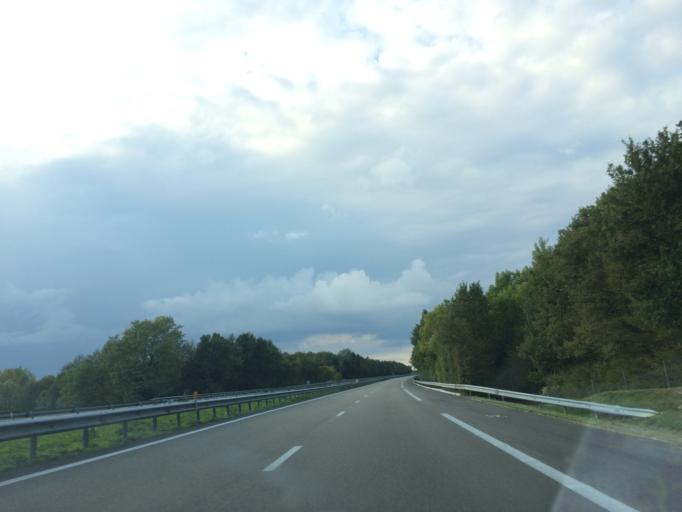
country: FR
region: Ile-de-France
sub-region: Departement de Seine-et-Marne
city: Egreville
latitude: 48.1394
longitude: 2.9154
